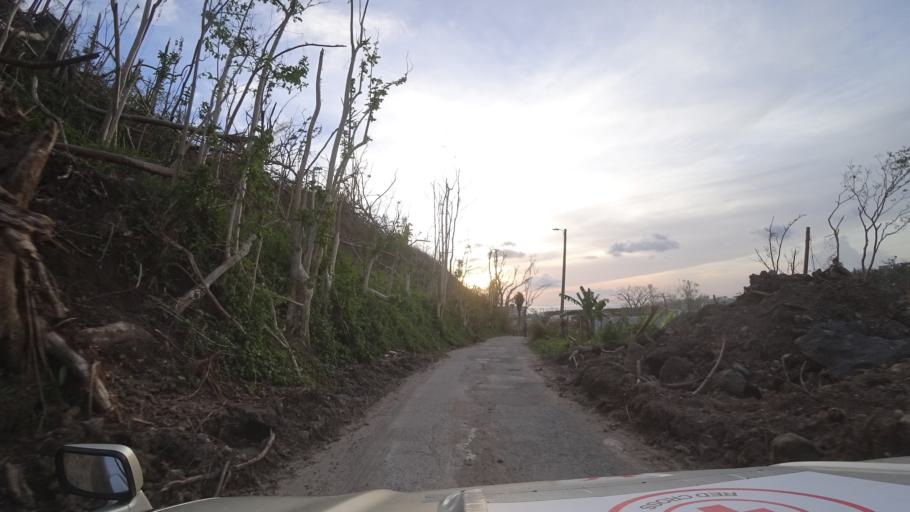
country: DM
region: Saint George
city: Roseau
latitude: 15.3009
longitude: -61.3802
